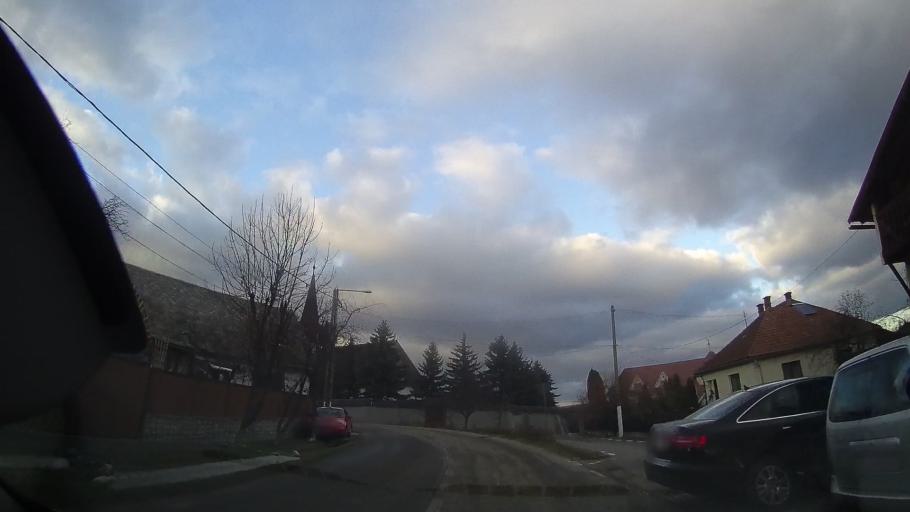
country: RO
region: Cluj
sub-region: Comuna Sancraiu
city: Sancraiu
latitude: 46.8281
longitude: 22.9884
